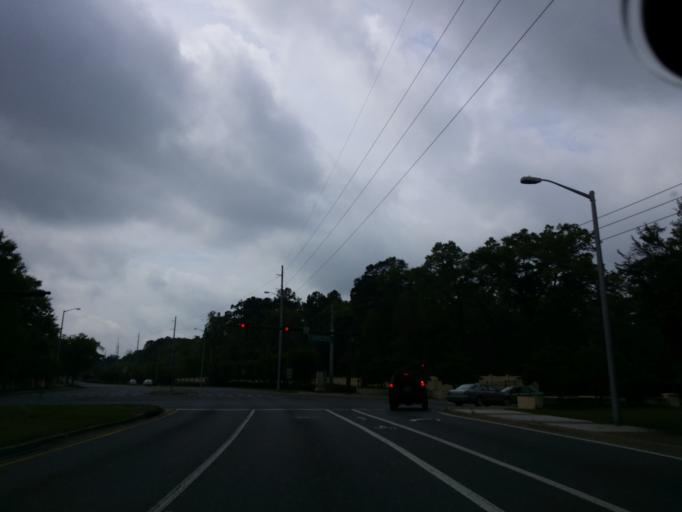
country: US
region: Florida
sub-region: Leon County
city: Tallahassee
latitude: 30.4737
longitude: -84.2436
